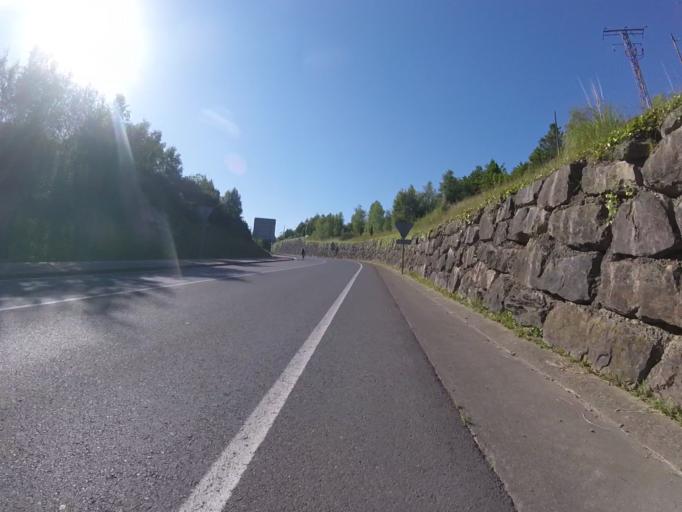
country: ES
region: Basque Country
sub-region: Provincia de Guipuzcoa
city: Azpeitia
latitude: 43.1765
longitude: -2.2613
